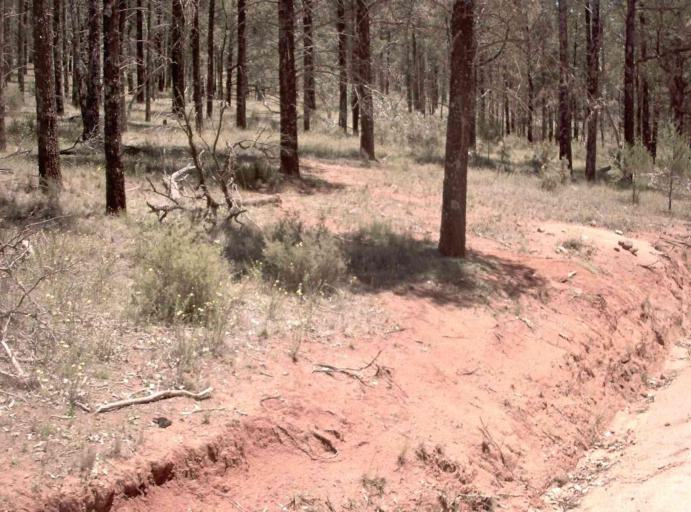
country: AU
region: New South Wales
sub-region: Snowy River
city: Jindabyne
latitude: -36.8934
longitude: 148.4227
